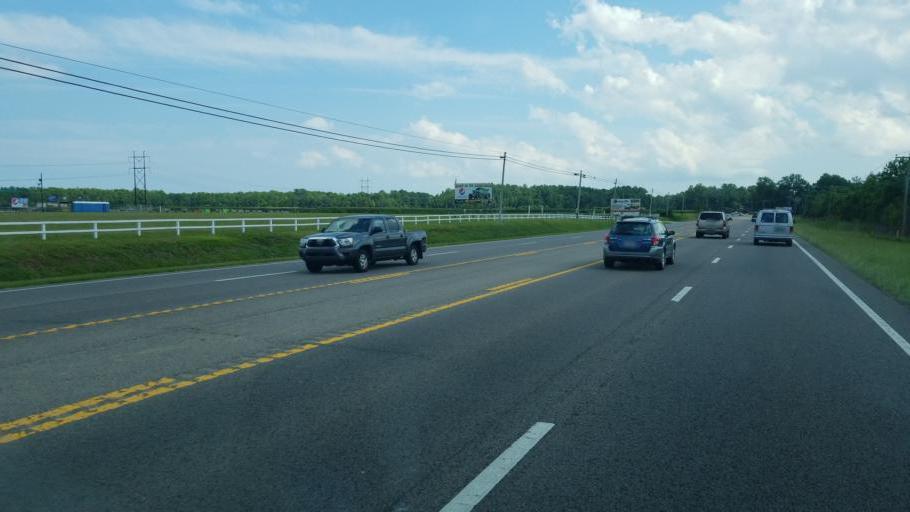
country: US
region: North Carolina
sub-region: Currituck County
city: Currituck
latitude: 36.3105
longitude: -75.9330
